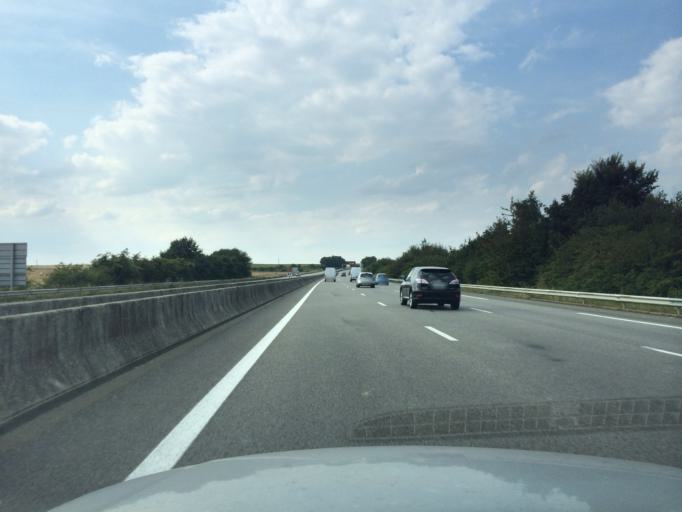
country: FR
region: Haute-Normandie
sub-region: Departement de l'Eure
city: Ande
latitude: 49.1655
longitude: 1.2570
